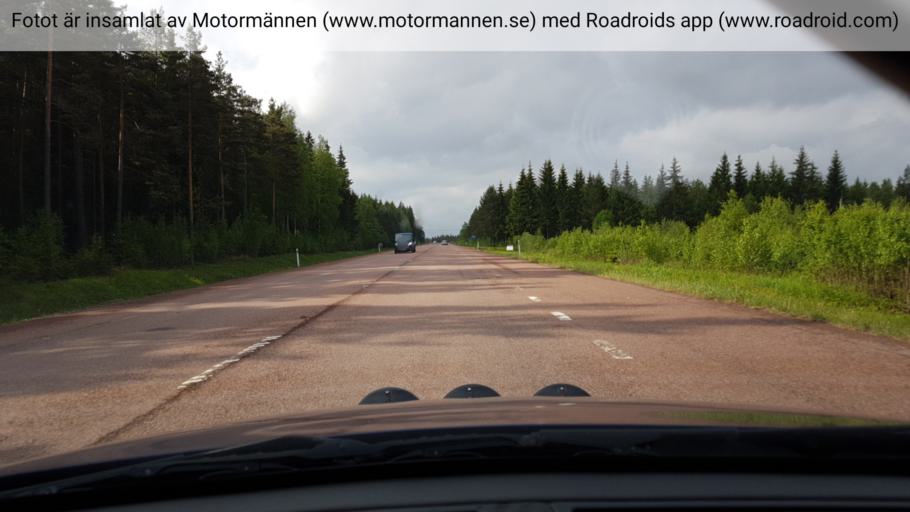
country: SE
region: Dalarna
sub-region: Mora Kommun
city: Mora
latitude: 61.0285
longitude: 14.5905
